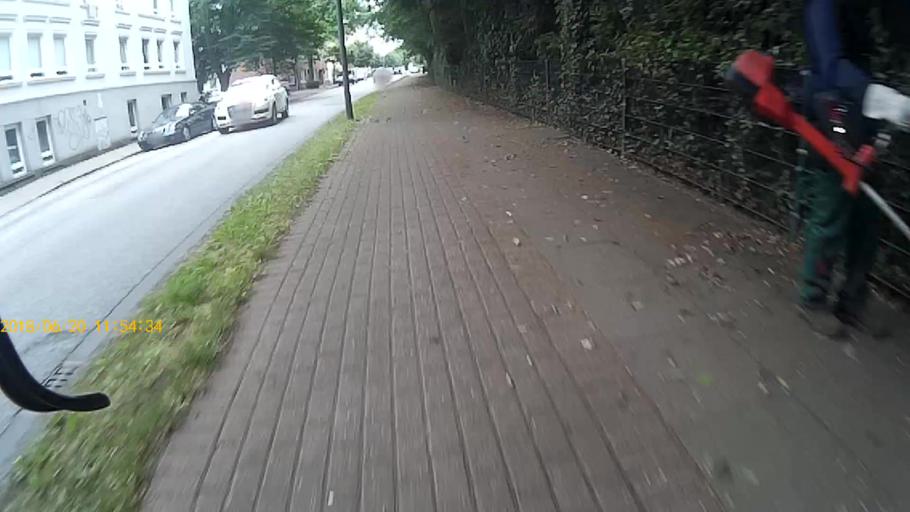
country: DE
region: Hamburg
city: Rothenburgsort
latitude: 53.5152
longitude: 10.0205
